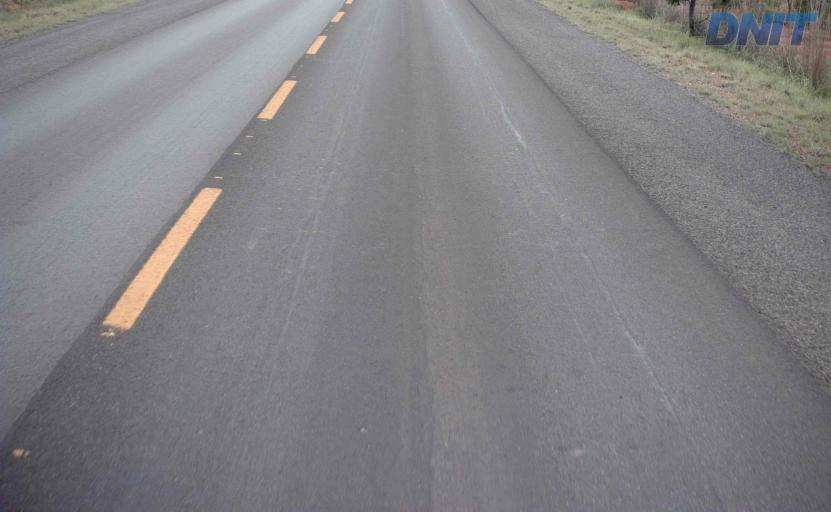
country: BR
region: Goias
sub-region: Padre Bernardo
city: Padre Bernardo
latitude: -15.2149
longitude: -48.5577
